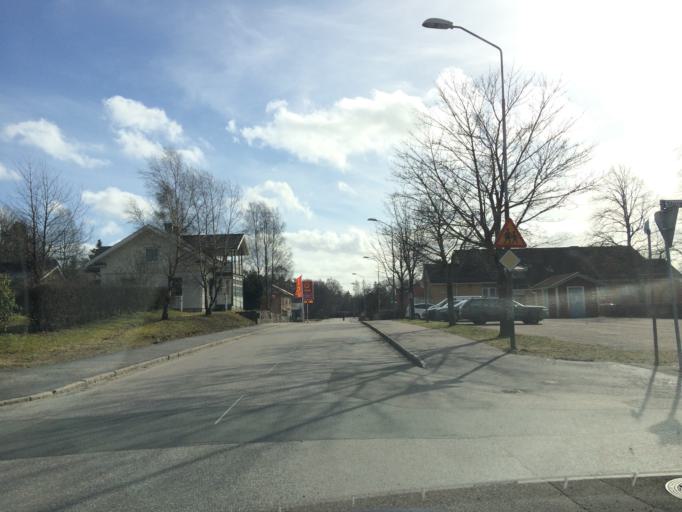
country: SE
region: Halland
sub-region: Hylte Kommun
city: Hyltebruk
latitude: 56.8286
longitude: 13.4390
